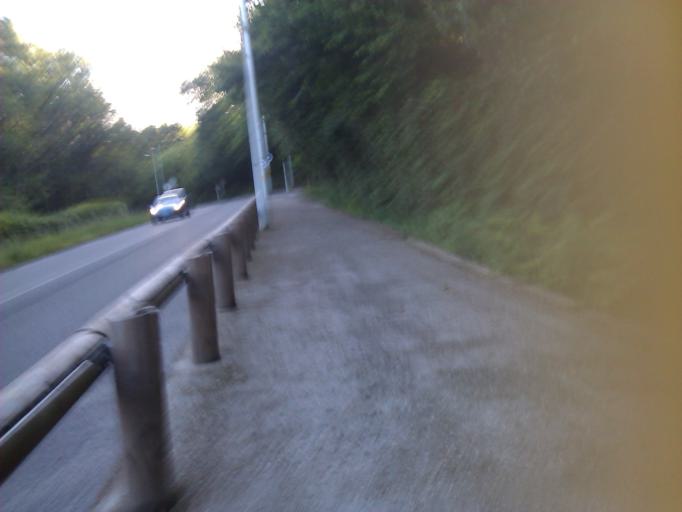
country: FR
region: Aquitaine
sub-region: Departement des Pyrenees-Atlantiques
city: Hendaye
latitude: 43.3761
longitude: -1.7501
